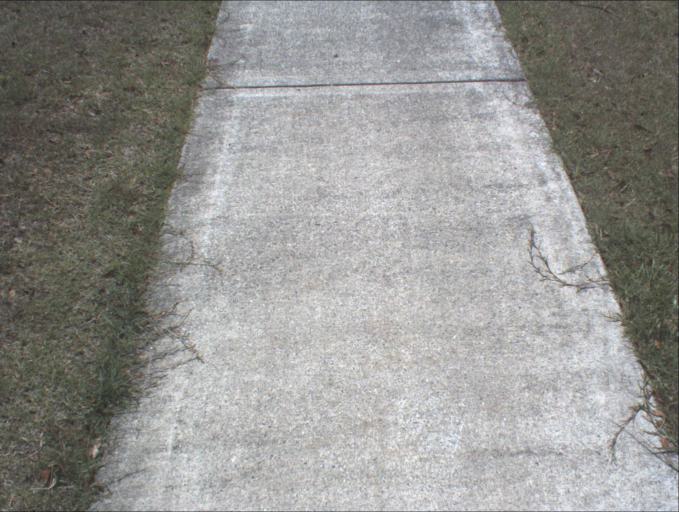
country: AU
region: Queensland
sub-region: Logan
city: Slacks Creek
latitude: -27.6697
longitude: 153.1523
